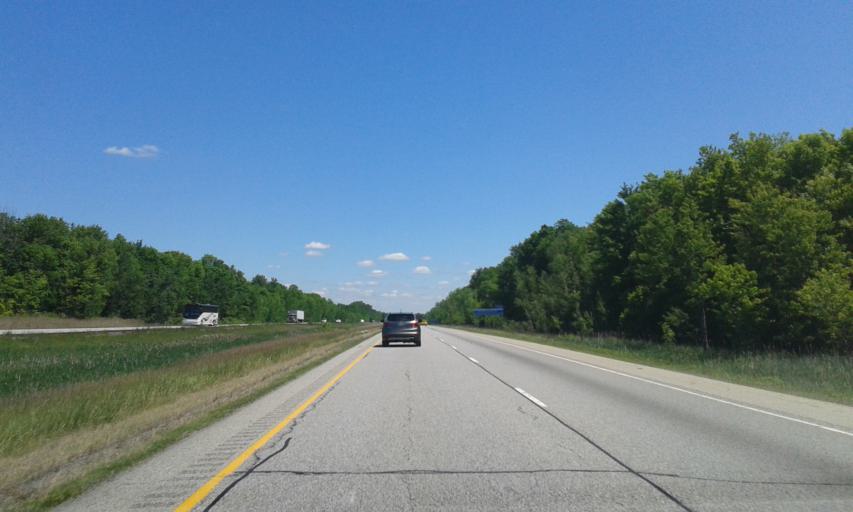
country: US
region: New York
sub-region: St. Lawrence County
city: Norfolk
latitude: 44.9051
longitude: -75.2259
